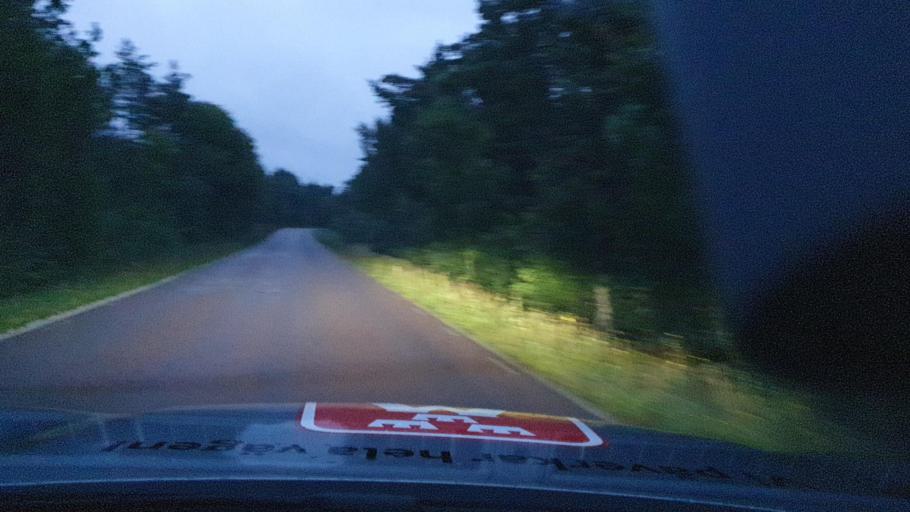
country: SE
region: Gotland
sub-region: Gotland
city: Slite
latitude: 57.7613
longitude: 18.8272
